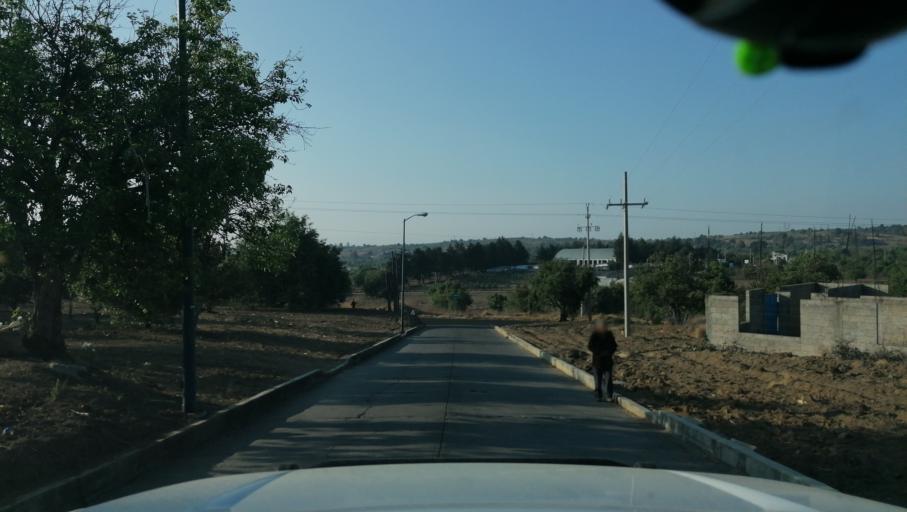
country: MX
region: Puebla
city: San Andres Calpan
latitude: 19.1057
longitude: -98.4403
